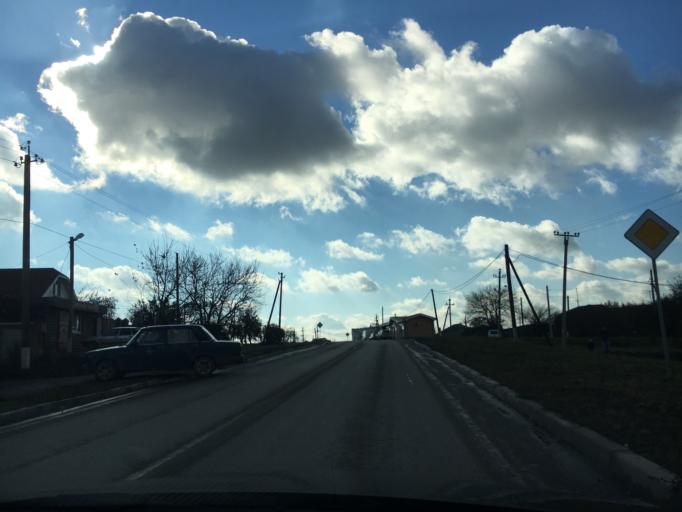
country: RU
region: Rostov
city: Matveyev Kurgan
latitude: 47.5601
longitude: 38.8721
